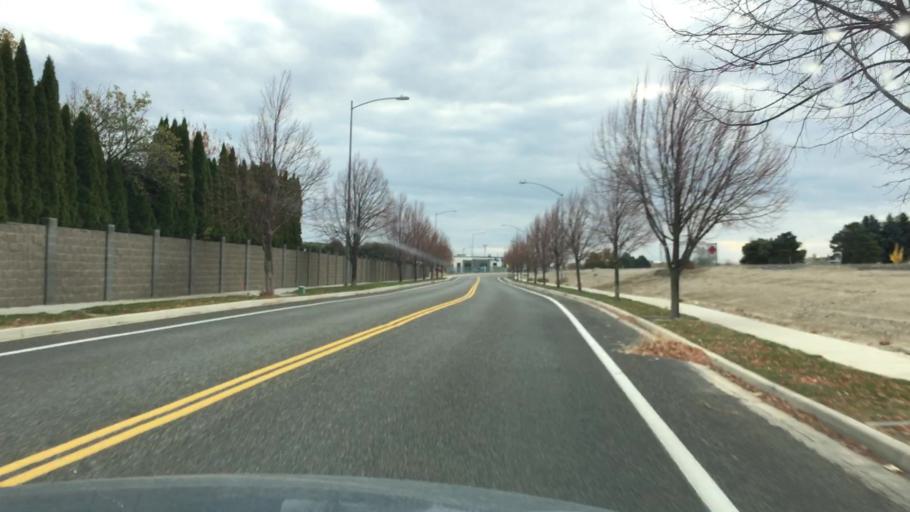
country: US
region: Washington
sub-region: Benton County
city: Kennewick
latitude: 46.1862
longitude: -119.1863
